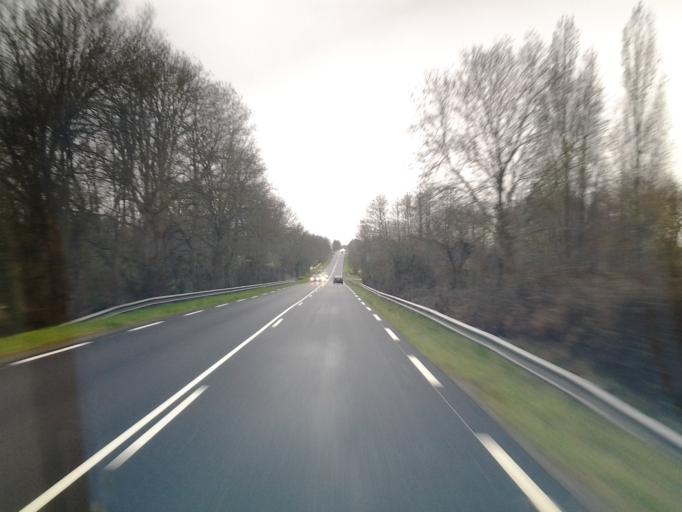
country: FR
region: Pays de la Loire
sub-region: Departement de la Vendee
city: Les Clouzeaux
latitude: 46.6540
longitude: -1.4939
